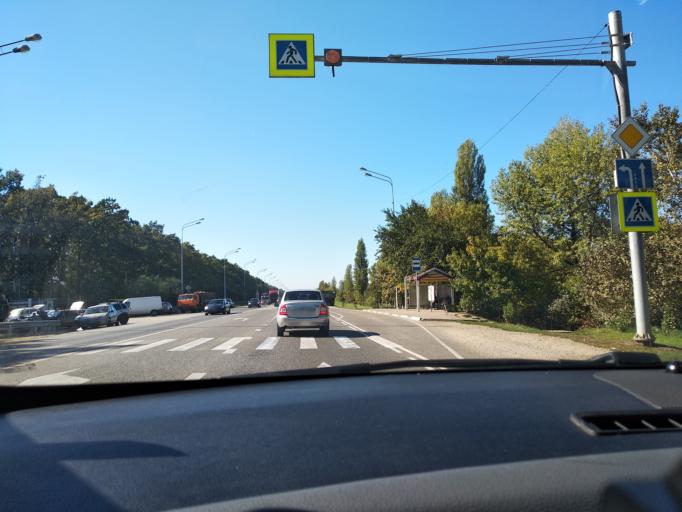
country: RU
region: Krasnodarskiy
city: Novotitarovskaya
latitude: 45.1437
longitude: 39.0450
